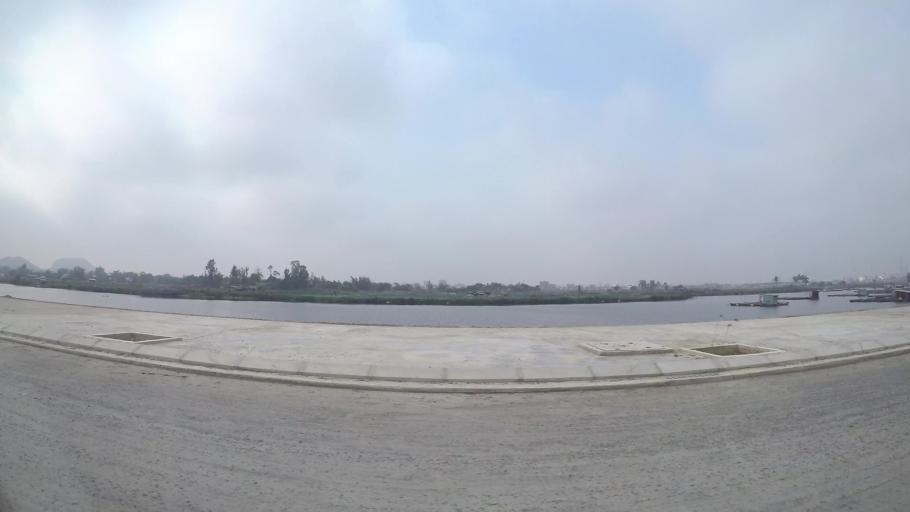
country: VN
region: Da Nang
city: Ngu Hanh Son
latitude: 16.0196
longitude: 108.2454
